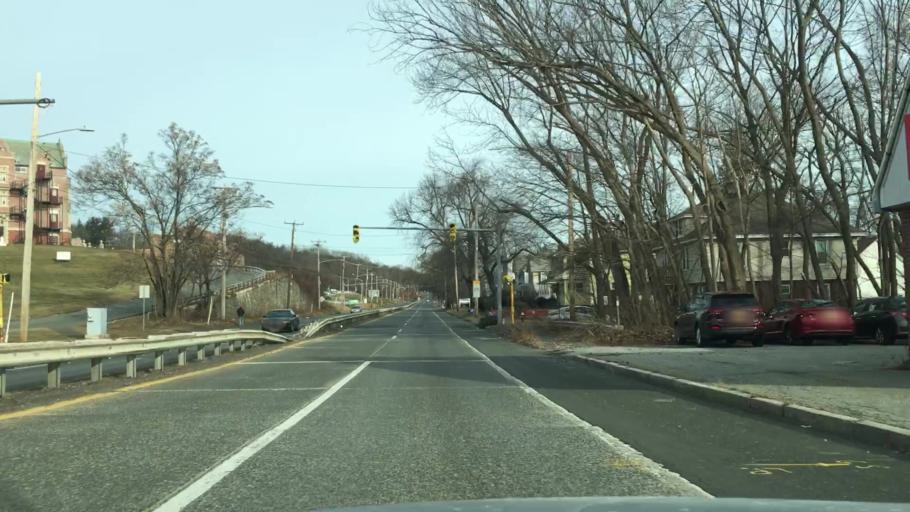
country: US
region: Massachusetts
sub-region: Hampden County
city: Chicopee
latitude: 42.1621
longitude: -72.6330
